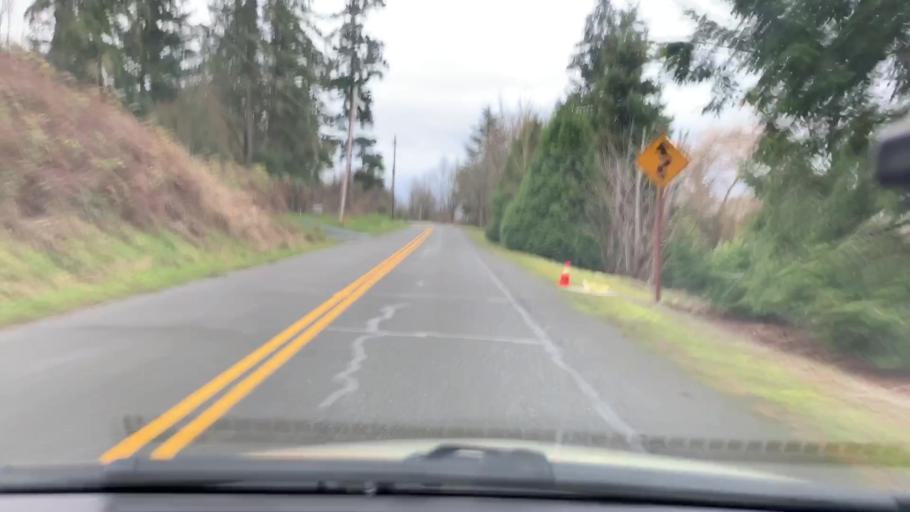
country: US
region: Washington
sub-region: King County
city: Redmond
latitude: 47.7080
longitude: -122.1344
